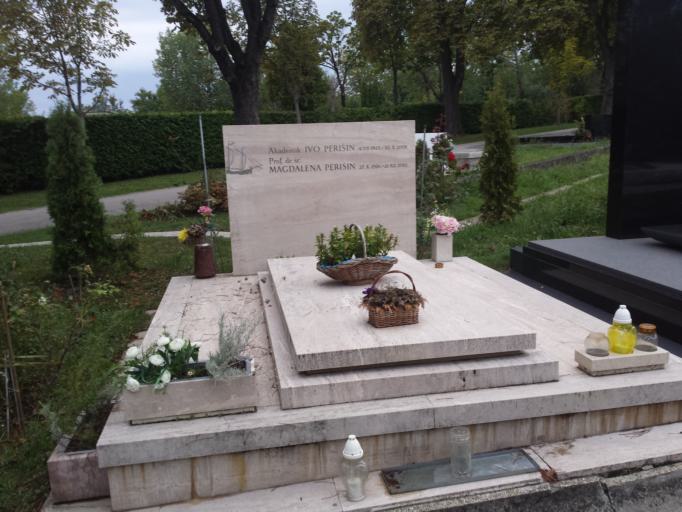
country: HR
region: Grad Zagreb
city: Zagreb
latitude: 45.8396
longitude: 15.9833
